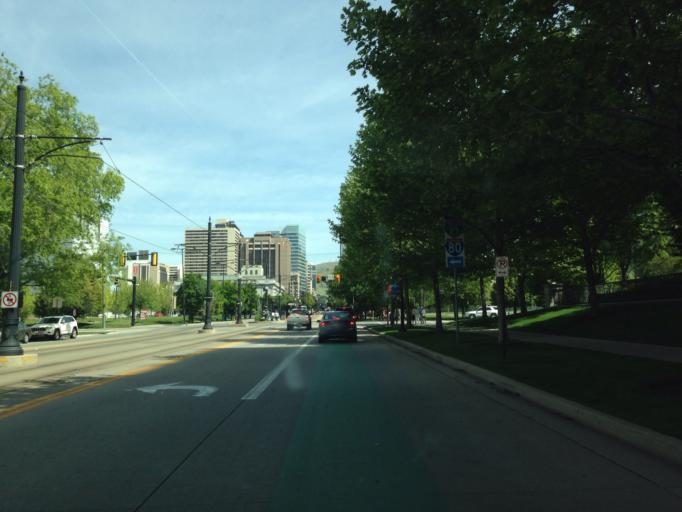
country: US
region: Utah
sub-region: Salt Lake County
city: Salt Lake City
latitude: 40.7577
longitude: -111.8910
